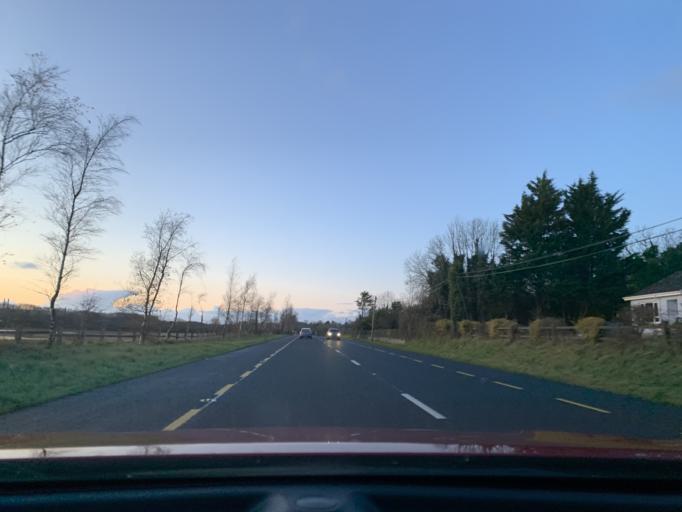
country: IE
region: Connaught
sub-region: County Leitrim
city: Carrick-on-Shannon
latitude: 53.9145
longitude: -7.9722
